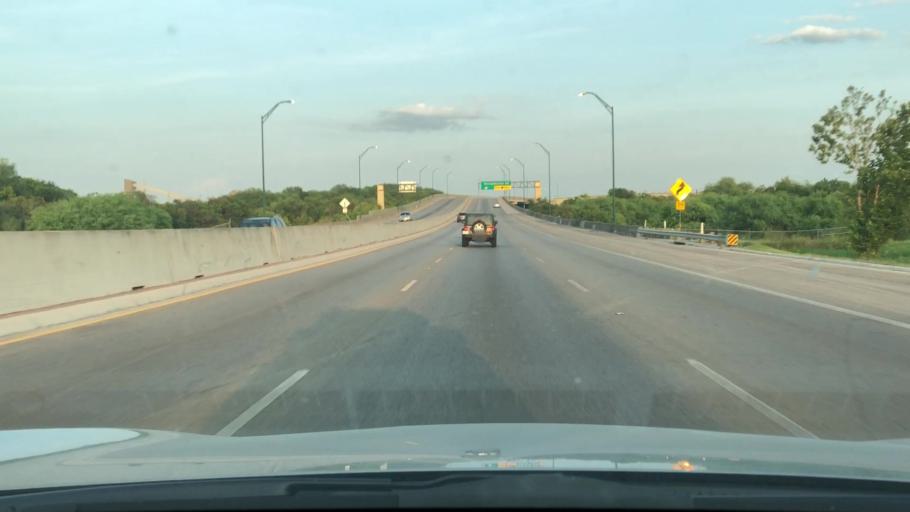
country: US
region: Texas
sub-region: Bexar County
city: Windcrest
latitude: 29.5464
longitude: -98.4306
